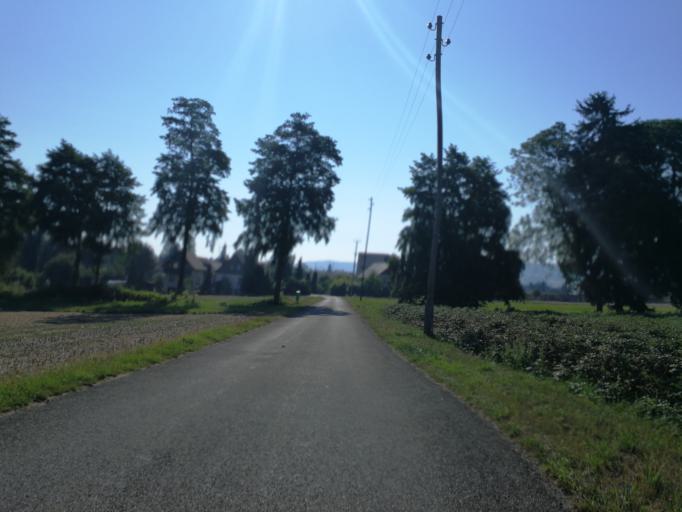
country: CH
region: Thurgau
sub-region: Frauenfeld District
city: Wagenhausen
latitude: 47.6591
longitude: 8.8435
